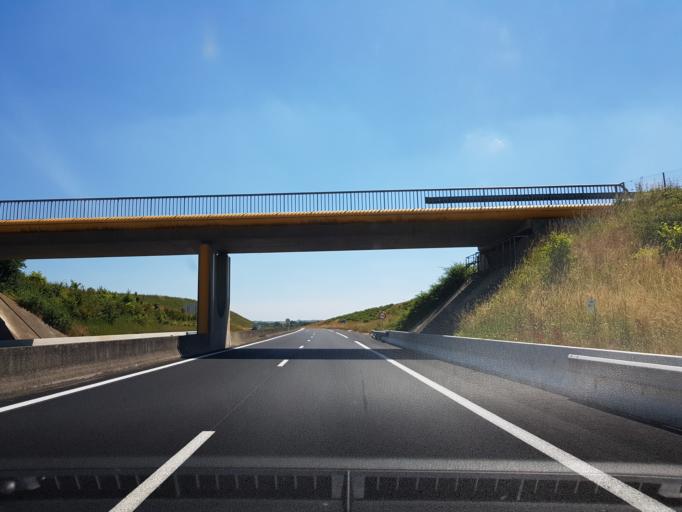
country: FR
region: Picardie
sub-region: Departement de la Somme
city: Nesle
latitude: 49.8351
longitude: 2.9071
